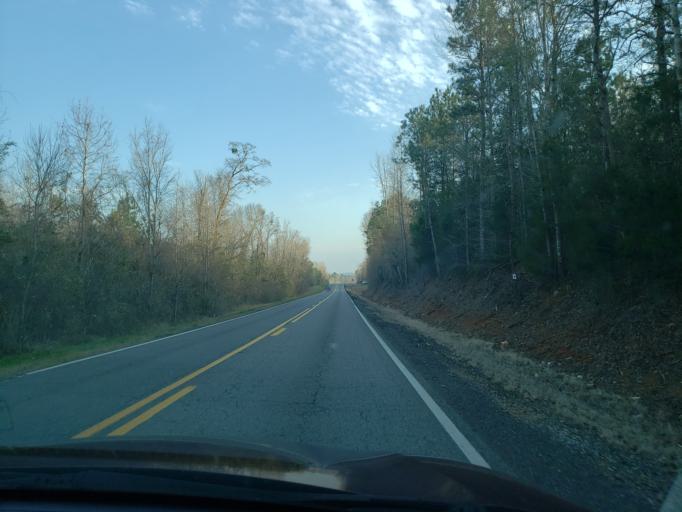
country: US
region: Alabama
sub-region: Hale County
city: Greensboro
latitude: 32.7815
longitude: -87.5881
